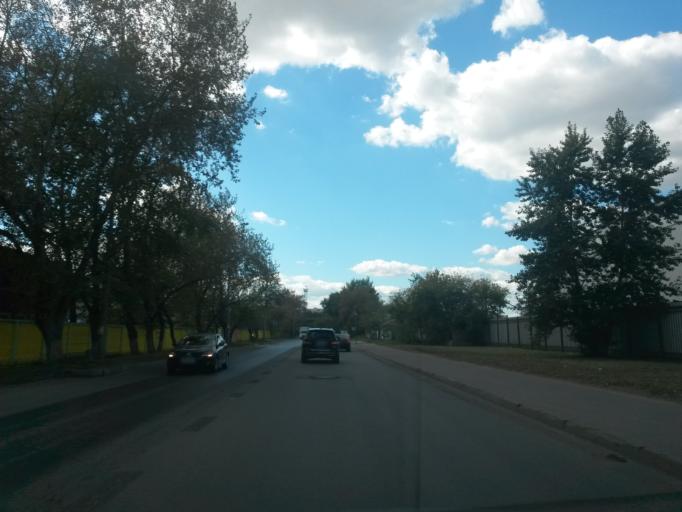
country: RU
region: Moscow
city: Tekstil'shchiki
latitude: 55.7038
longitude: 37.7065
